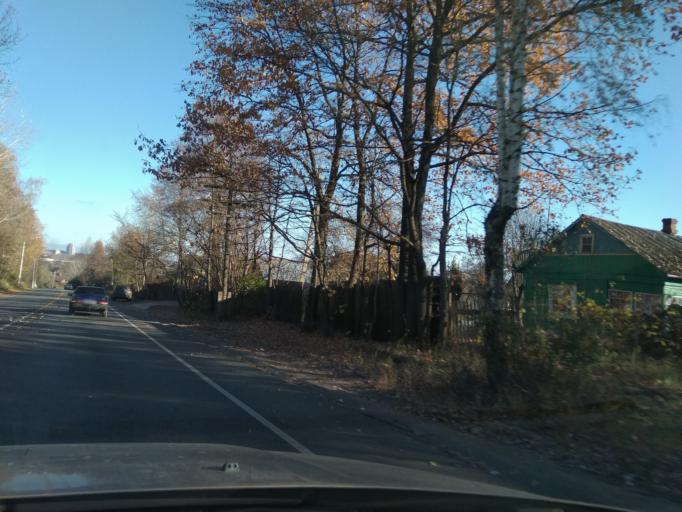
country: RU
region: Moskovskaya
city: Istra
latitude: 55.8842
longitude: 36.8595
